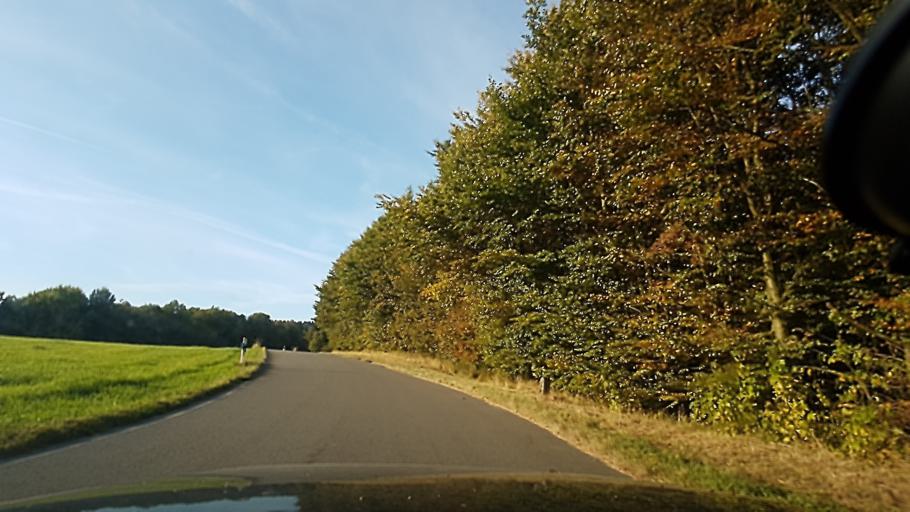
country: DE
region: North Rhine-Westphalia
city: Kierspe
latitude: 51.0942
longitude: 7.5998
